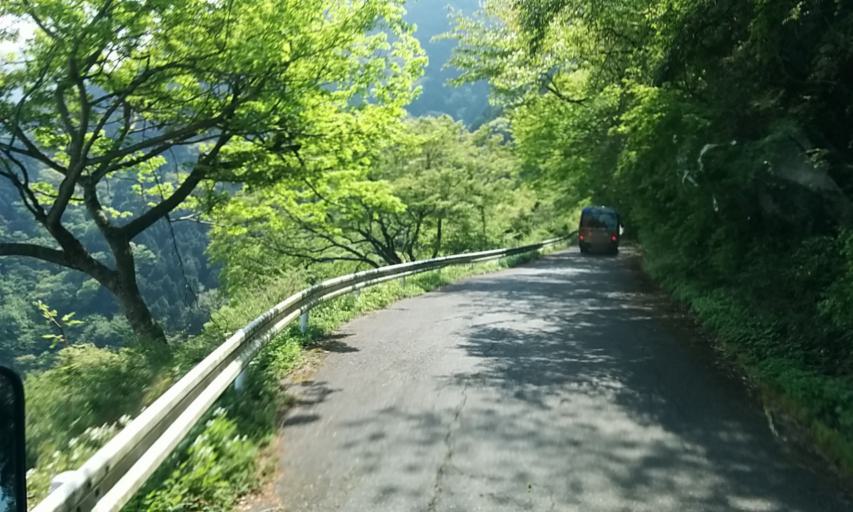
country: JP
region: Ehime
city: Niihama
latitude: 33.8750
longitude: 133.3021
